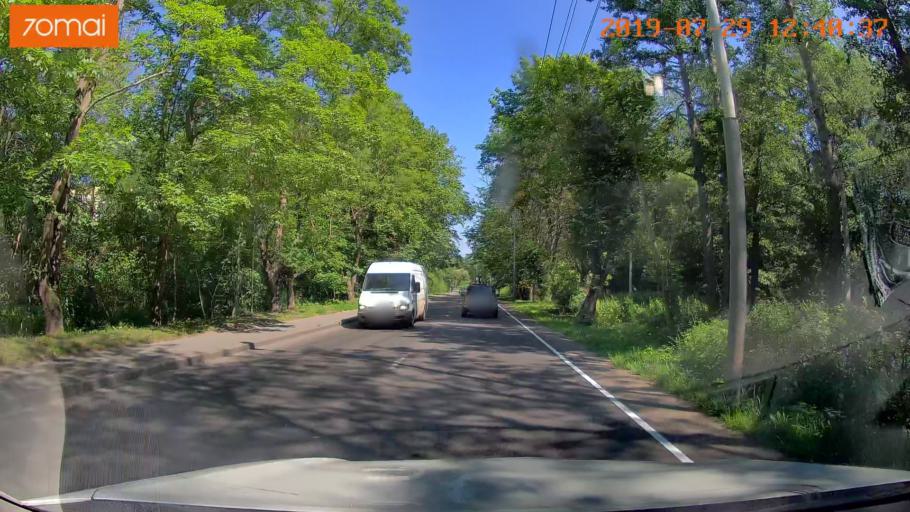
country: RU
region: Kaliningrad
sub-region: Gorod Kaliningrad
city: Kaliningrad
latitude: 54.6683
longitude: 20.5443
